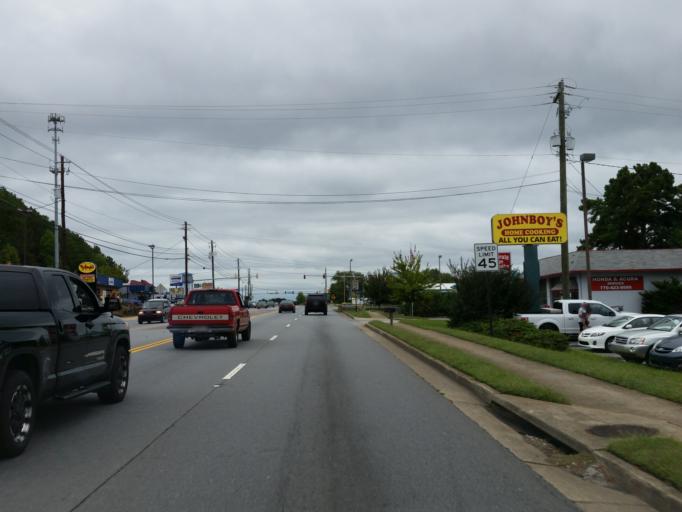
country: US
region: Georgia
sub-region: Cherokee County
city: Woodstock
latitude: 34.0268
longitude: -84.5283
